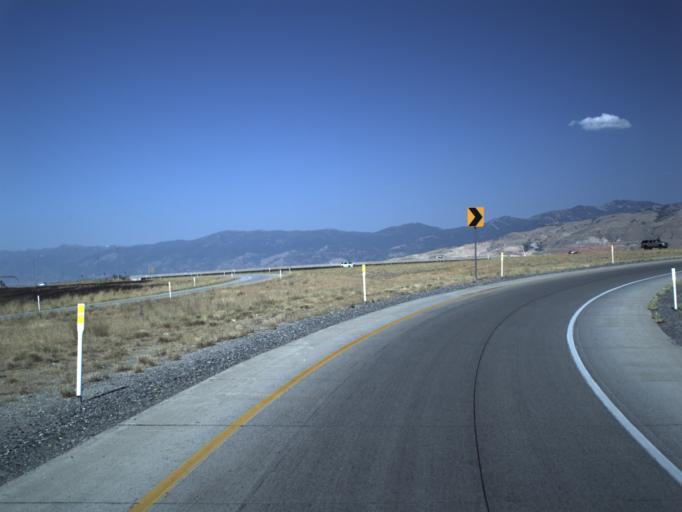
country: US
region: Utah
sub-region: Salt Lake County
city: West Valley City
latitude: 40.7662
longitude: -111.9890
